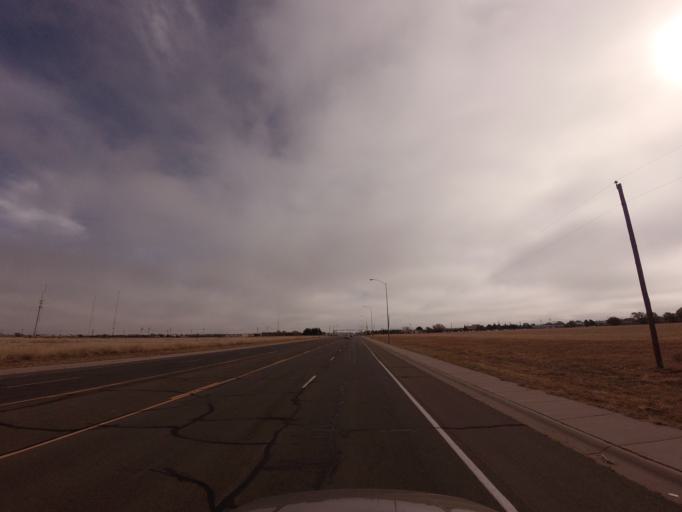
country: US
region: New Mexico
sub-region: Curry County
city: Clovis
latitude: 34.4339
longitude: -103.2176
